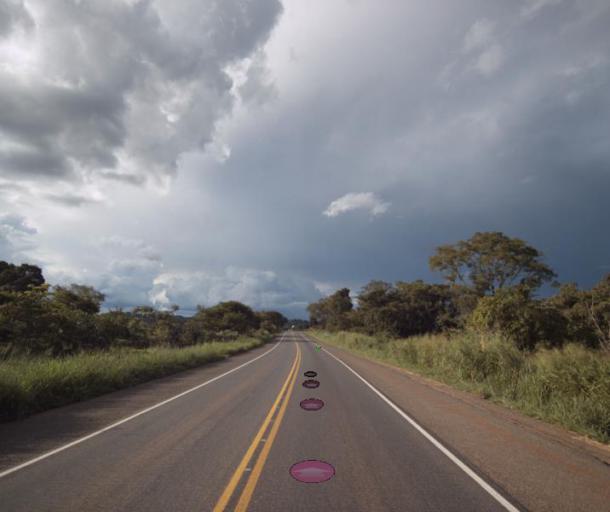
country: BR
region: Goias
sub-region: Rialma
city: Rialma
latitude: -15.2744
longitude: -49.5510
